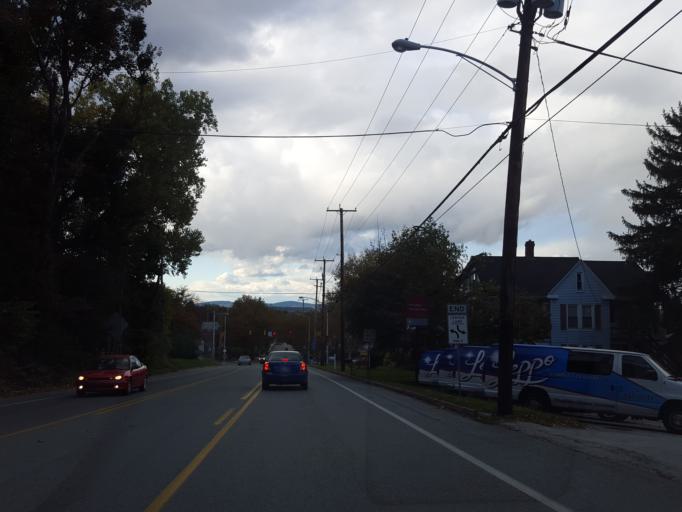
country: US
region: Pennsylvania
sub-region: York County
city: Valley View
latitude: 39.9475
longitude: -76.7108
